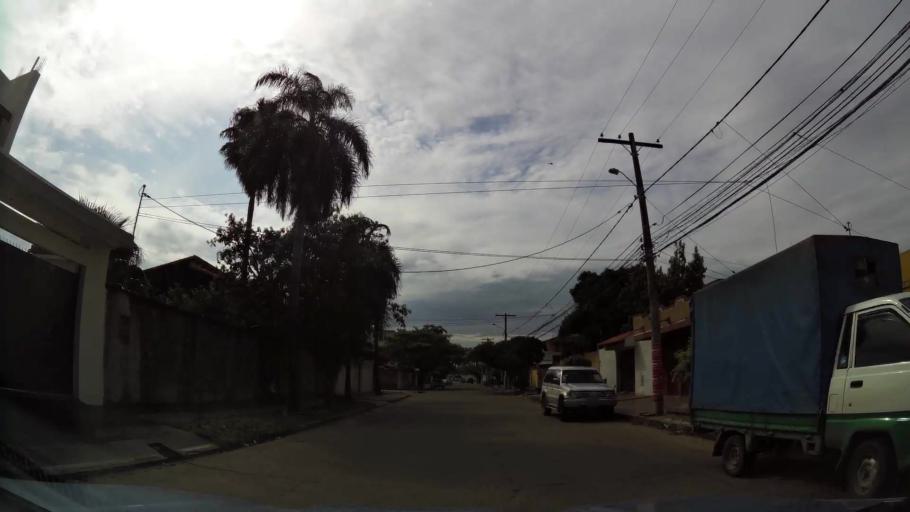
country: BO
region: Santa Cruz
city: Santa Cruz de la Sierra
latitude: -17.7870
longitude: -63.1997
